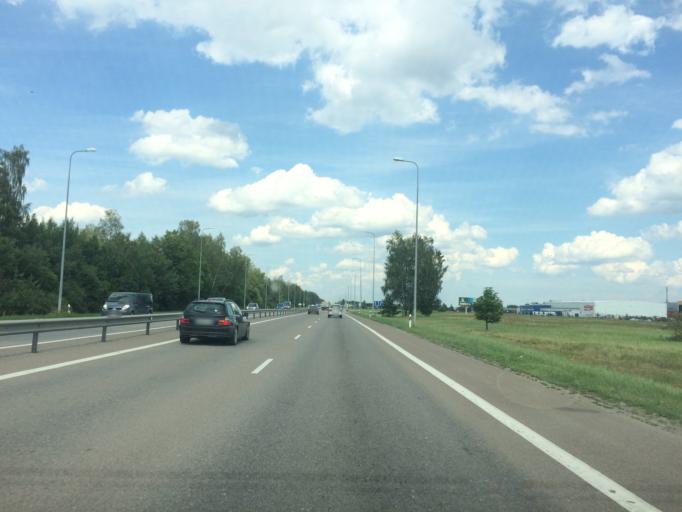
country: LT
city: Ramuciai
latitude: 54.9415
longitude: 24.0017
